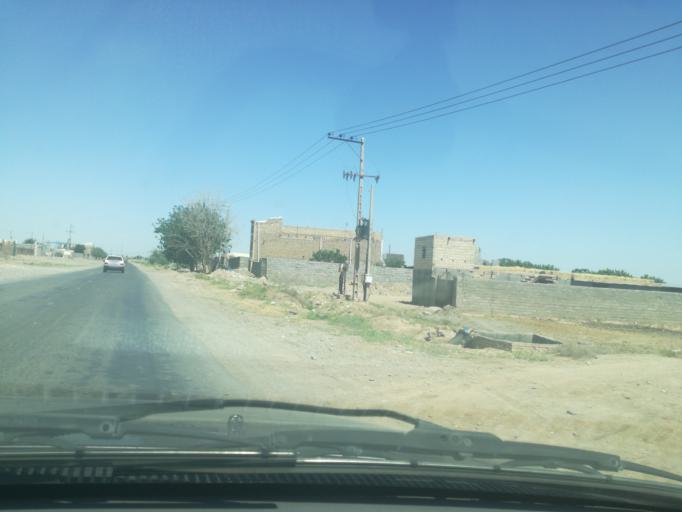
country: IR
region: Razavi Khorasan
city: Sarakhs
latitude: 36.5627
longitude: 61.1465
